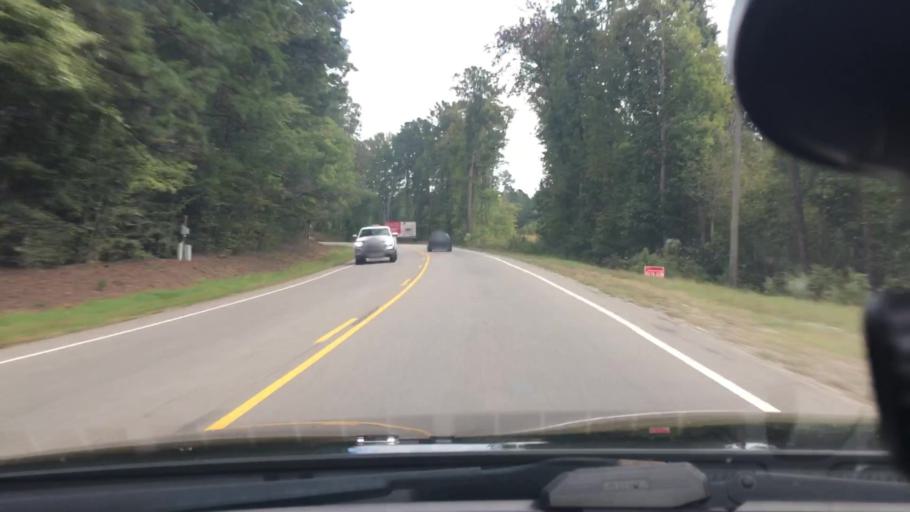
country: US
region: North Carolina
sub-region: Moore County
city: Carthage
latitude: 35.3630
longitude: -79.4421
